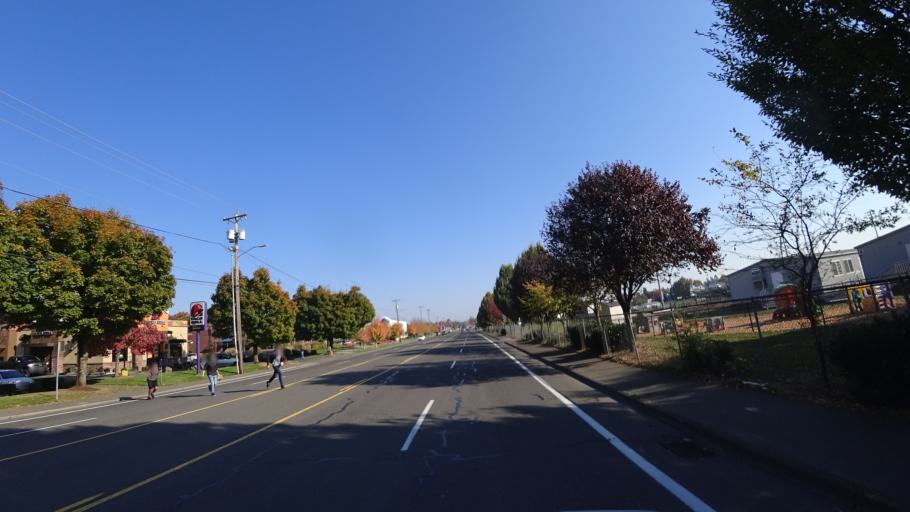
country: US
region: Oregon
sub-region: Multnomah County
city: Gresham
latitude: 45.5084
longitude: -122.4297
